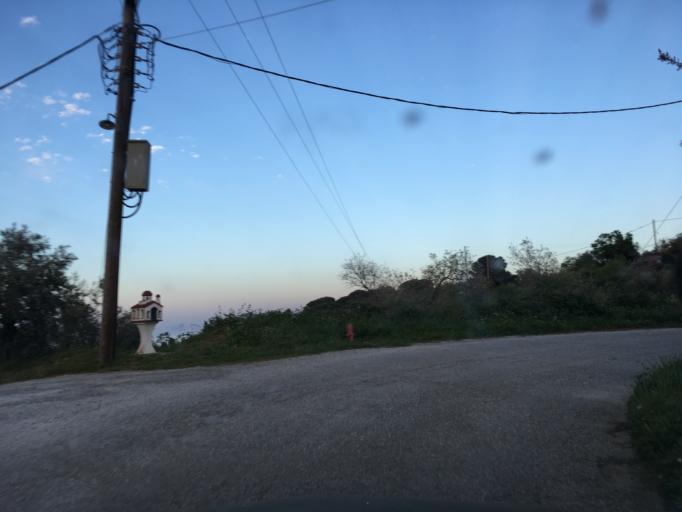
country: GR
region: Thessaly
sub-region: Nomos Magnisias
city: Skopelos
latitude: 39.1820
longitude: 23.6218
